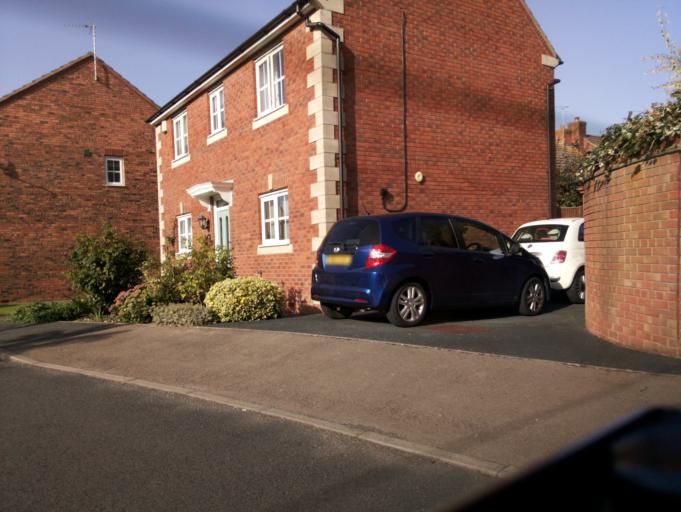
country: GB
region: England
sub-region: Gloucestershire
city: Tewkesbury
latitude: 51.9845
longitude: -2.1403
